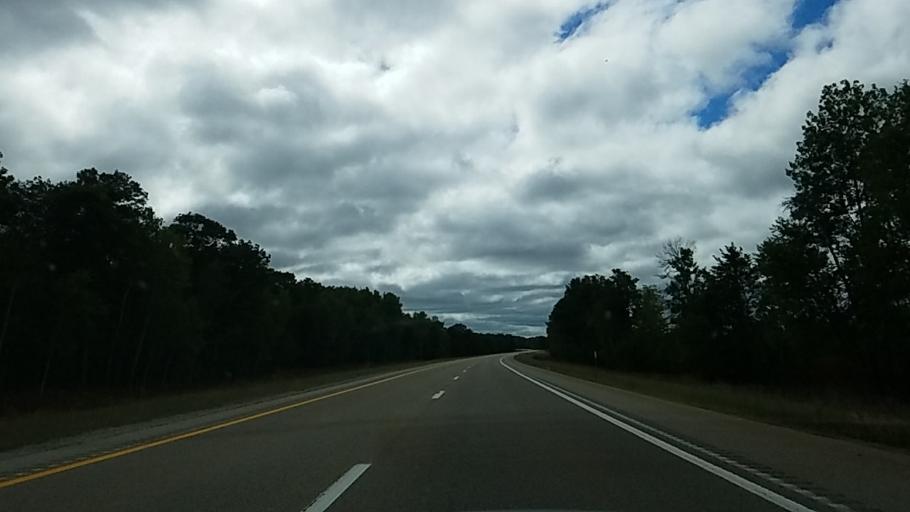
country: US
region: Michigan
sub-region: Crawford County
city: Grayling
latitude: 44.5690
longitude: -84.7088
